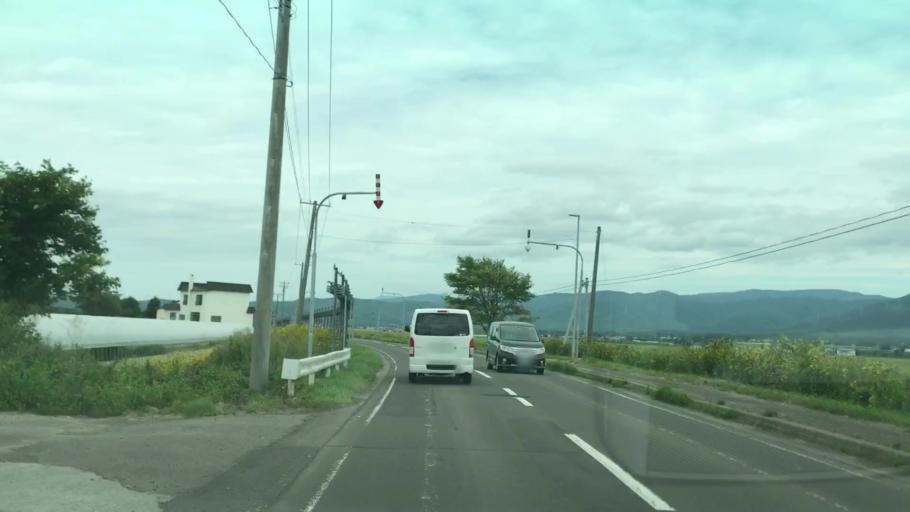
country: JP
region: Hokkaido
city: Iwanai
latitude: 43.0039
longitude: 140.5845
